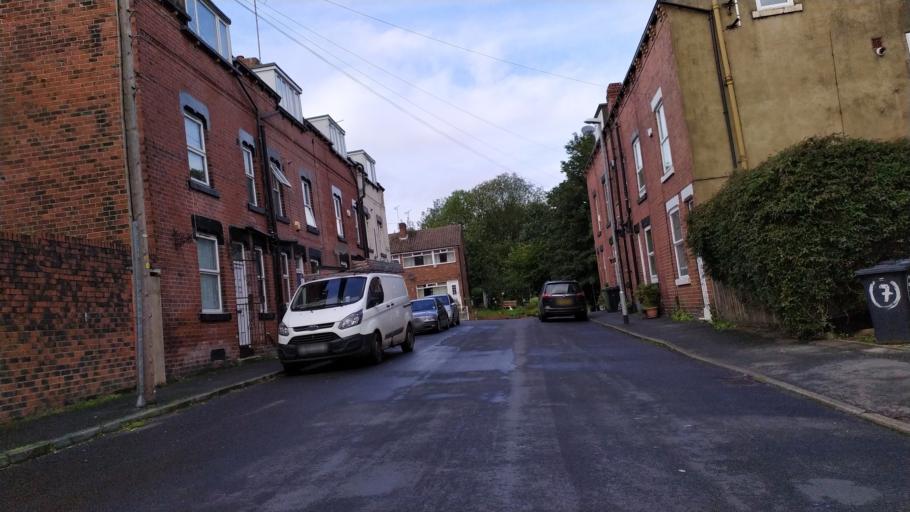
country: GB
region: England
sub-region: City and Borough of Leeds
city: Chapel Allerton
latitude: 53.8273
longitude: -1.5701
